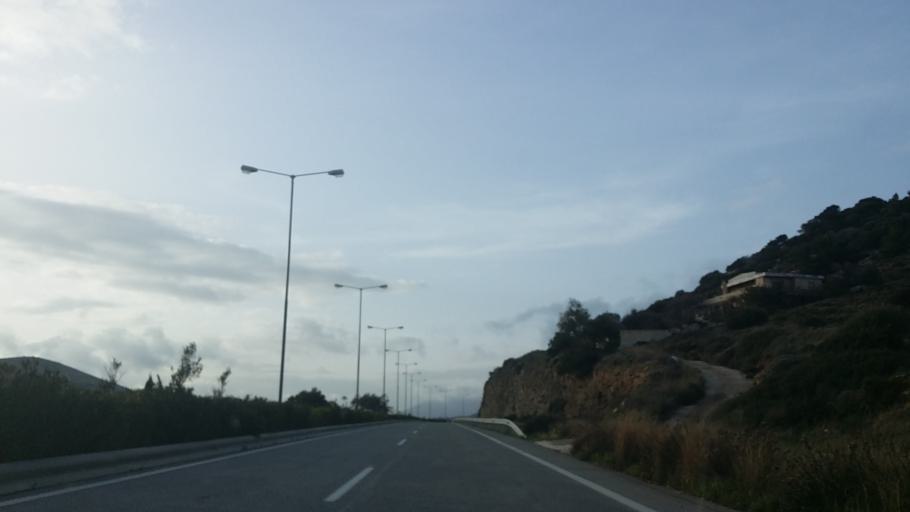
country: GR
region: Attica
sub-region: Nomarchia Anatolikis Attikis
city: Keratea
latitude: 37.7946
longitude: 24.0540
